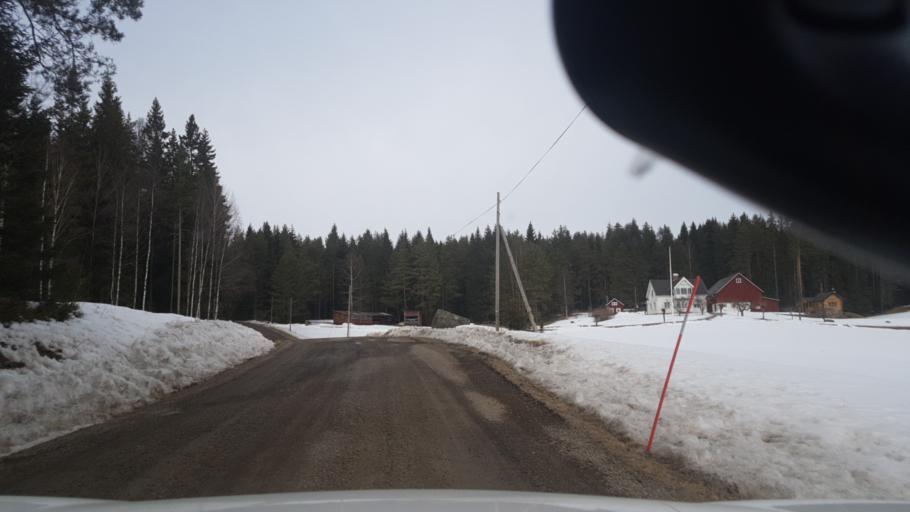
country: SE
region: Vaermland
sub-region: Eda Kommun
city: Amotfors
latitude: 59.8167
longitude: 12.4560
